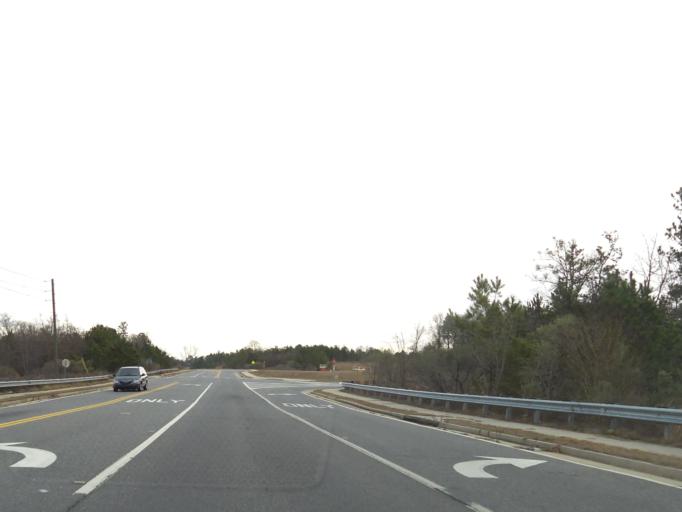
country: US
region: Georgia
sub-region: Peach County
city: Byron
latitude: 32.7375
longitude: -83.7179
